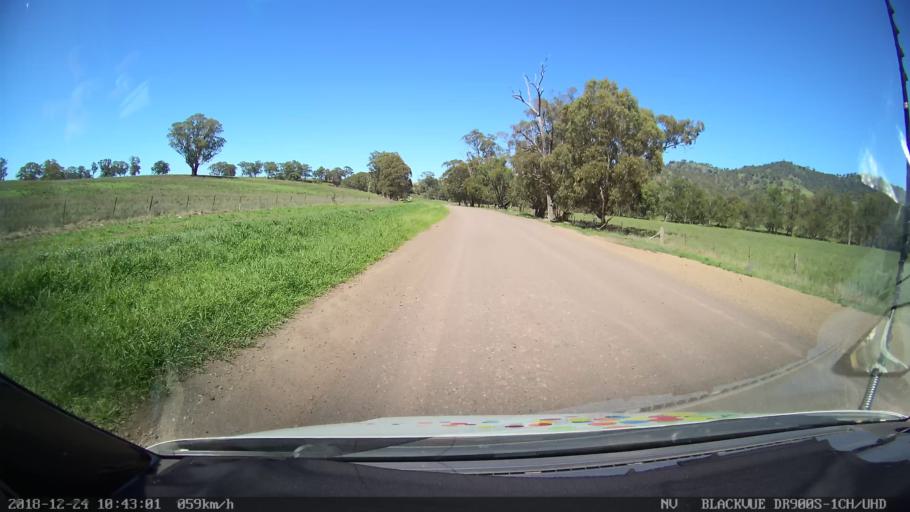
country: AU
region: New South Wales
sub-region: Upper Hunter Shire
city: Merriwa
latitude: -31.8799
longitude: 150.4490
